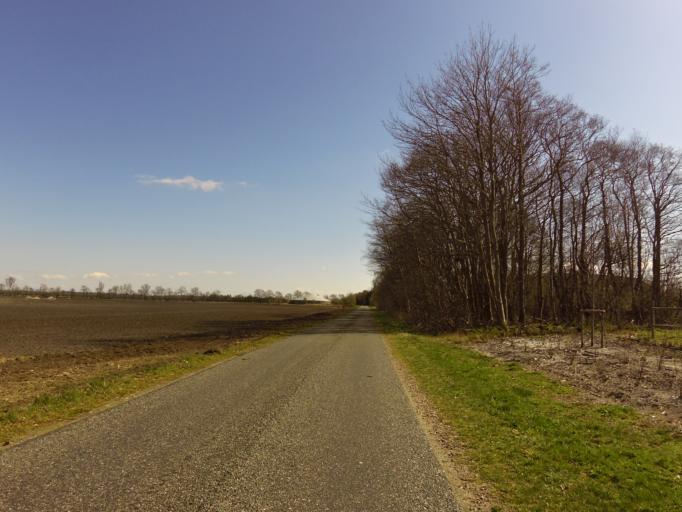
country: DK
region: South Denmark
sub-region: Esbjerg Kommune
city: Ribe
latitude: 55.3410
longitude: 8.8615
